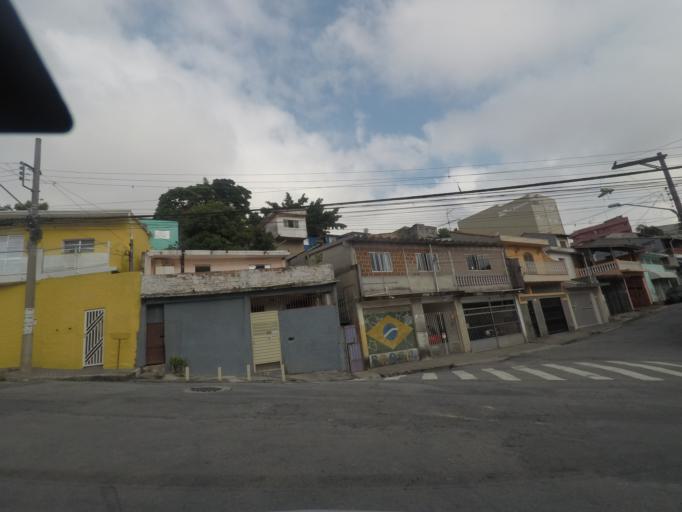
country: BR
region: Sao Paulo
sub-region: Osasco
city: Osasco
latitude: -23.5727
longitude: -46.7787
